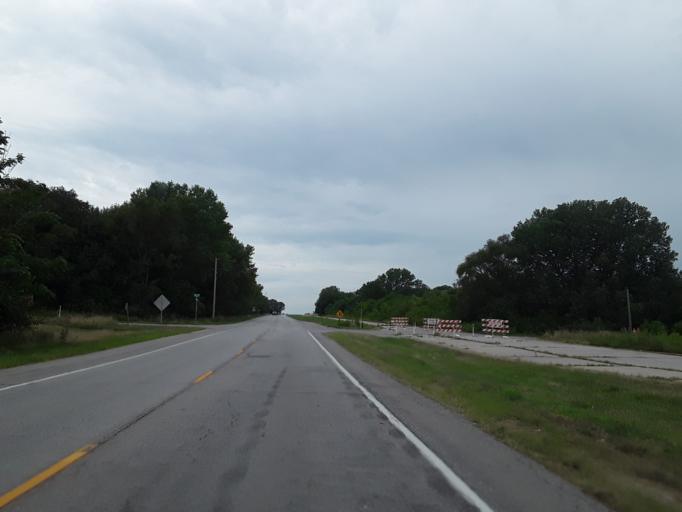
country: US
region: Nebraska
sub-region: Douglas County
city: Bennington
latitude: 41.3650
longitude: -96.0608
